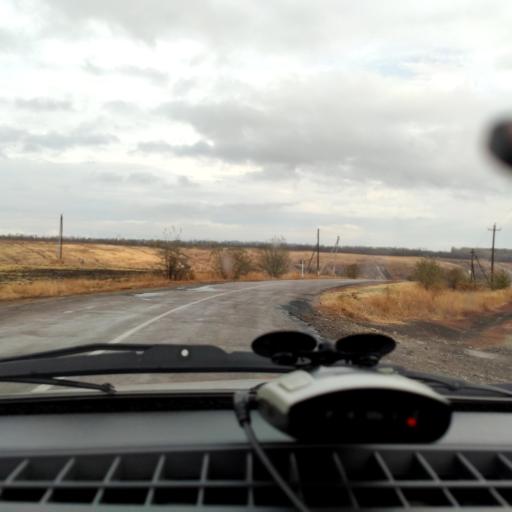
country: RU
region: Voronezj
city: Kolodeznyy
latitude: 51.2380
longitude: 39.0432
